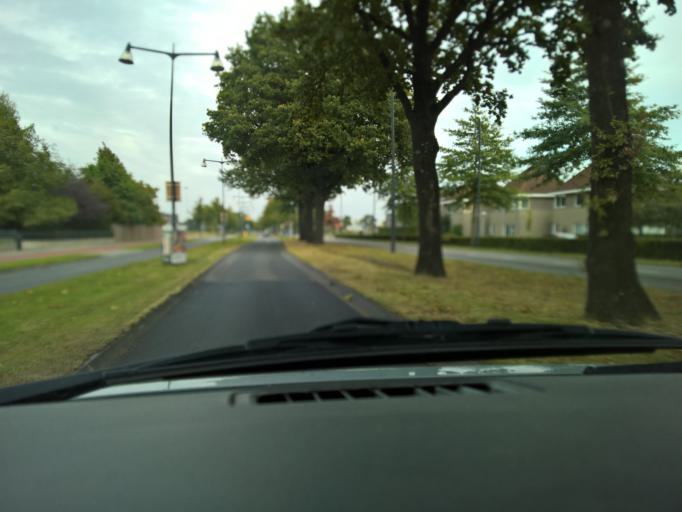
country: NL
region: North Brabant
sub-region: Gemeente Eindhoven
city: Meerhoven
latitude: 51.4342
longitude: 5.4077
